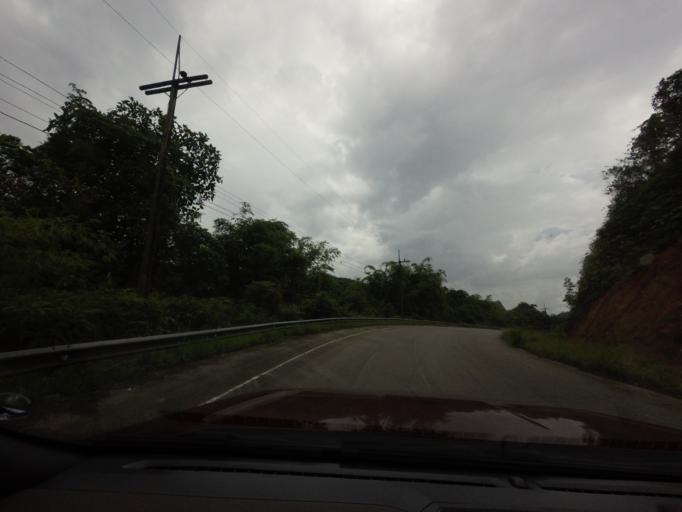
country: TH
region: Narathiwat
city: Sukhirin
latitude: 5.9806
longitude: 101.6937
